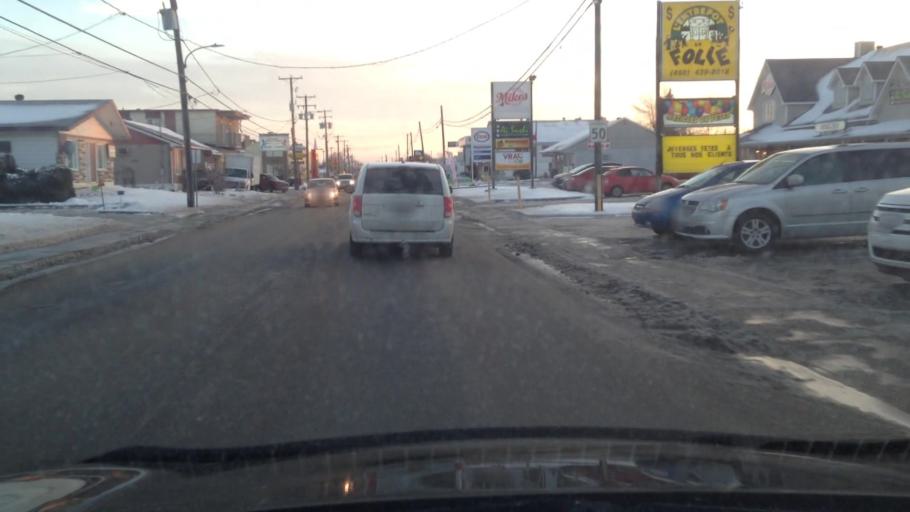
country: CA
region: Quebec
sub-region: Lanaudiere
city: Saint-Lin-Laurentides
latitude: 45.8648
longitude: -73.7572
